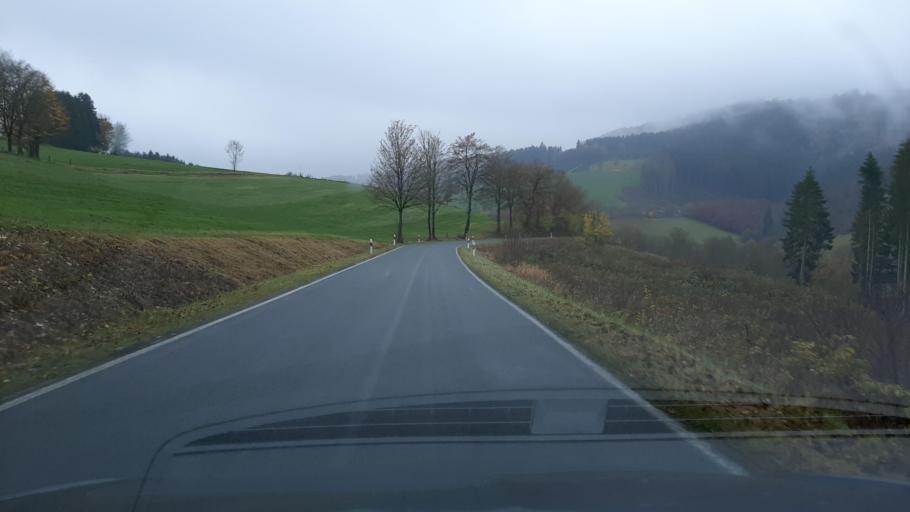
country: DE
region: North Rhine-Westphalia
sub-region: Regierungsbezirk Arnsberg
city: Olsberg
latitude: 51.2882
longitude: 8.4871
